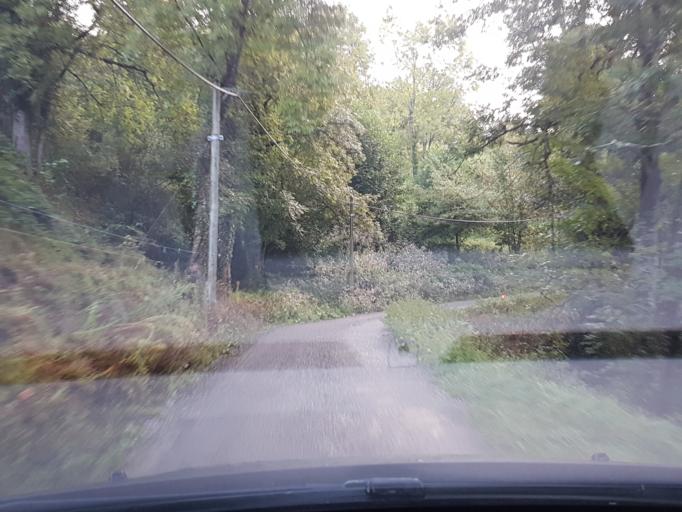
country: FR
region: Midi-Pyrenees
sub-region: Departement de l'Ariege
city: Montjoie-en-Couserans
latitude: 42.9025
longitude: 1.3533
